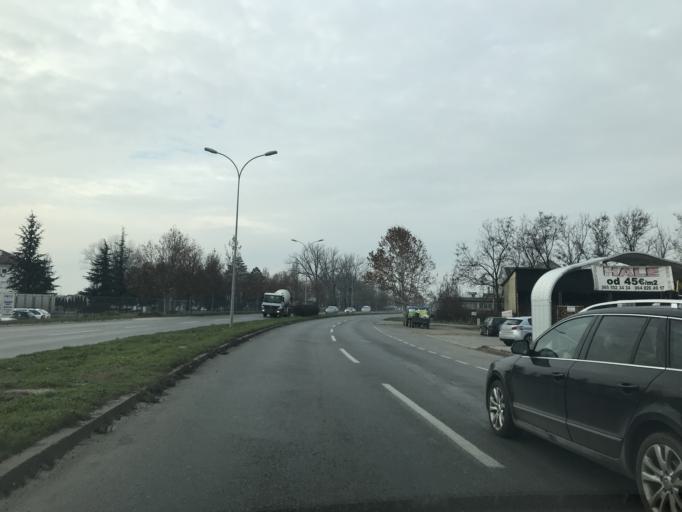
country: RS
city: Veternik
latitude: 45.2439
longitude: 19.7787
